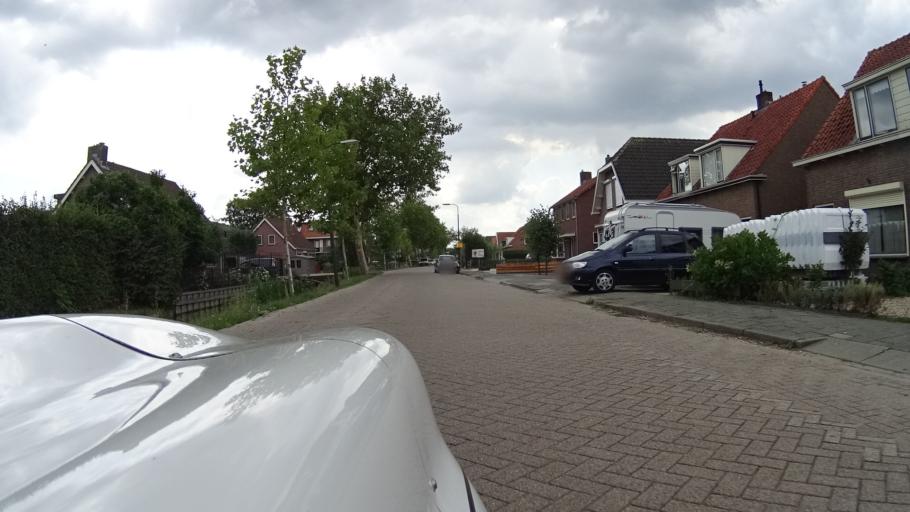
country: NL
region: South Holland
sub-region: Gemeente Hardinxveld-Giessendam
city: Boven-Hardinxveld
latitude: 51.8284
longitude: 4.8829
